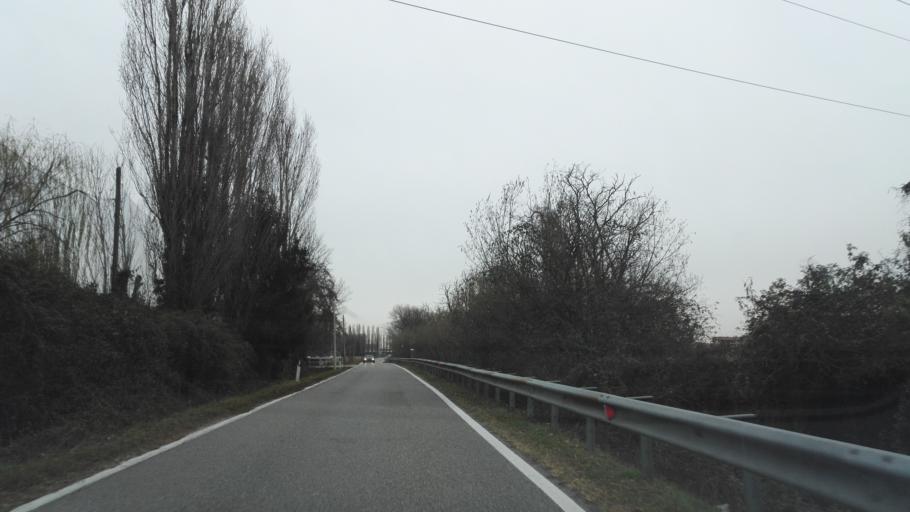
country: IT
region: Lombardy
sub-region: Citta metropolitana di Milano
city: Bettola-Zeloforomagno
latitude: 45.4430
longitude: 9.3161
